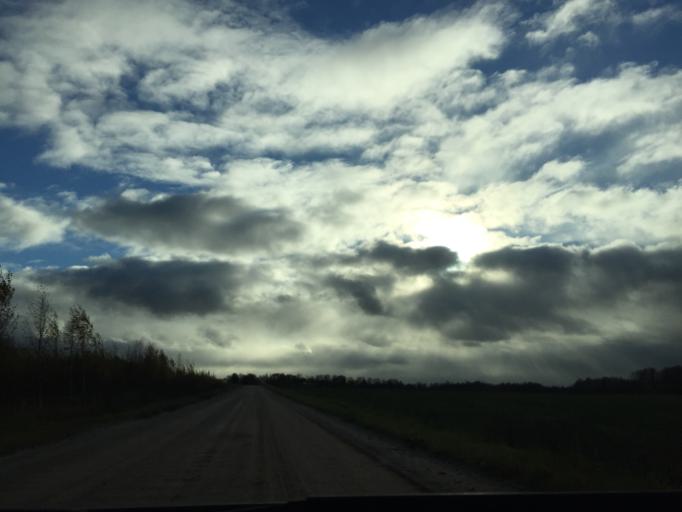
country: LV
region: Tukuma Rajons
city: Tukums
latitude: 56.9315
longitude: 22.9526
